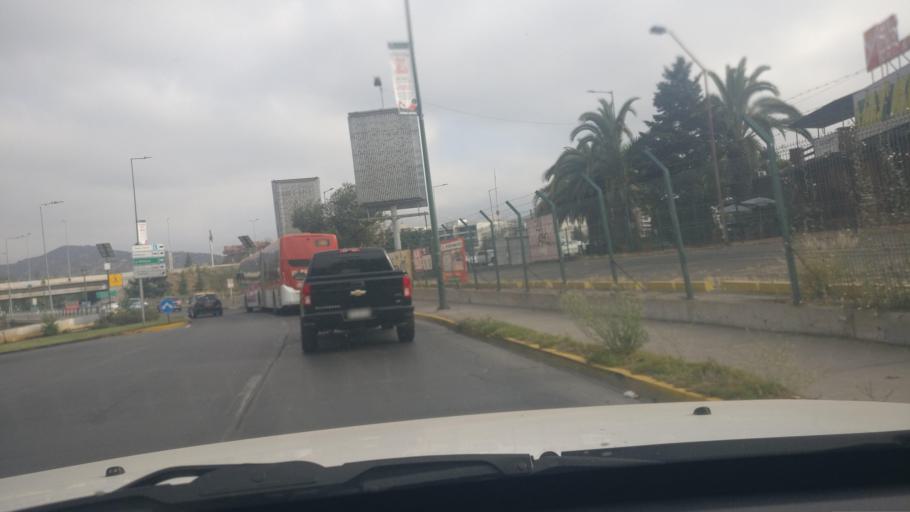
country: CL
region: Santiago Metropolitan
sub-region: Provincia de Santiago
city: Villa Presidente Frei, Nunoa, Santiago, Chile
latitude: -33.3709
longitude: -70.5185
